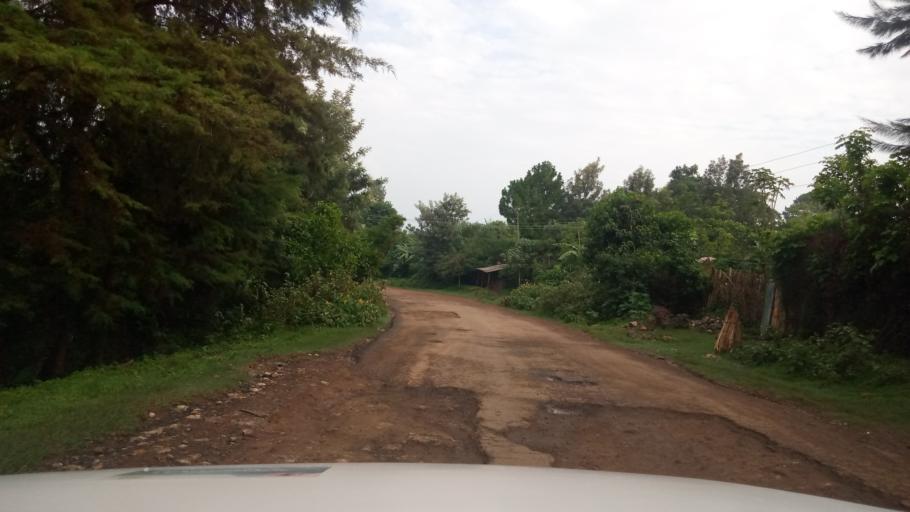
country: ET
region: Oromiya
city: Agaro
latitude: 7.7971
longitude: 36.7207
